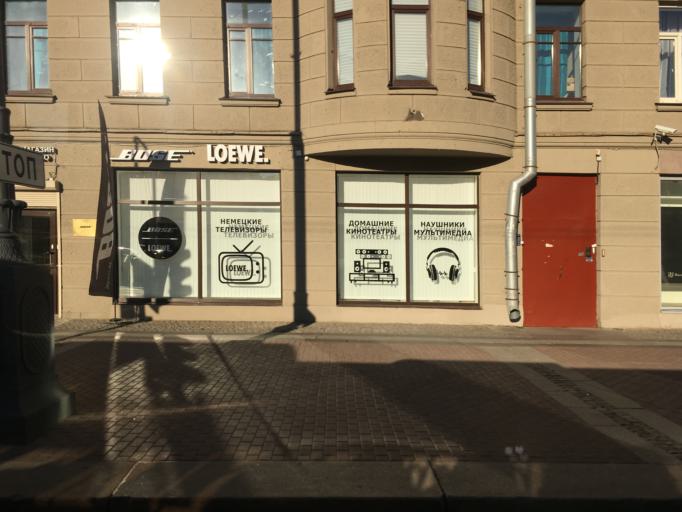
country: RU
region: St.-Petersburg
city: Admiralteisky
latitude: 59.8869
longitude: 30.3202
